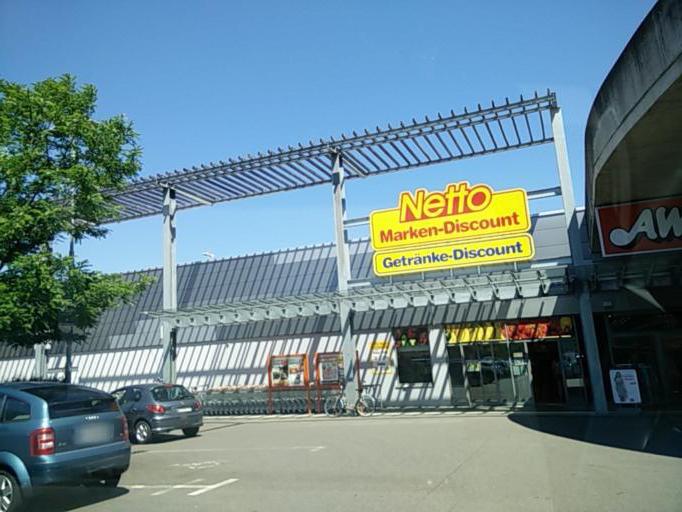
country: DE
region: Baden-Wuerttemberg
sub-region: Tuebingen Region
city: Tuebingen
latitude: 48.5148
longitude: 9.0695
